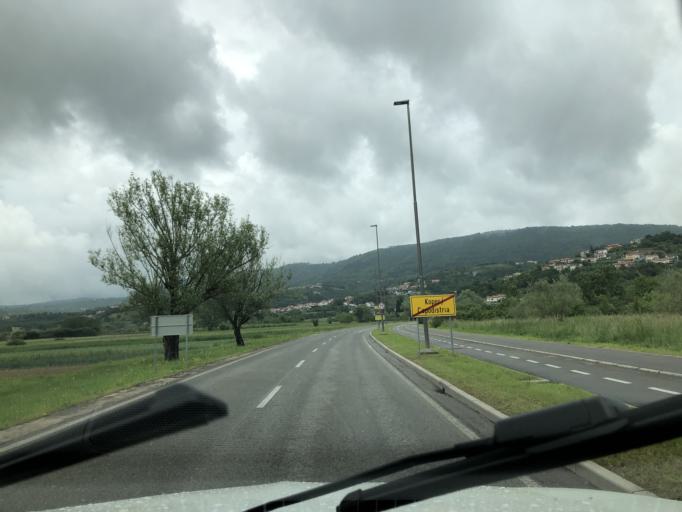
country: SI
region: Koper-Capodistria
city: Koper
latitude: 45.5219
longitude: 13.7422
